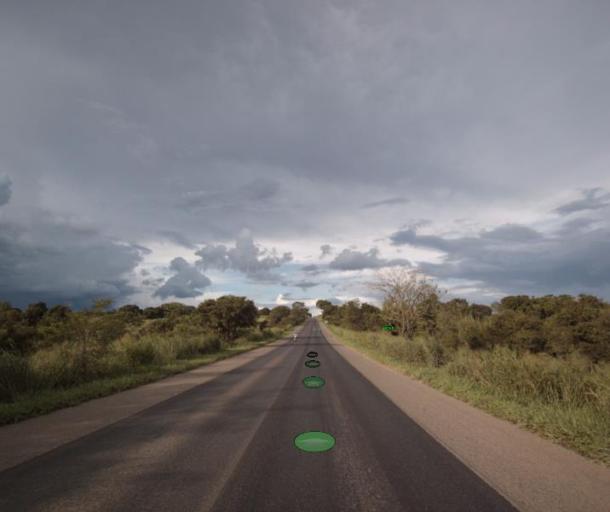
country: BR
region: Goias
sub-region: Itapaci
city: Itapaci
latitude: -15.1146
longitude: -49.4927
